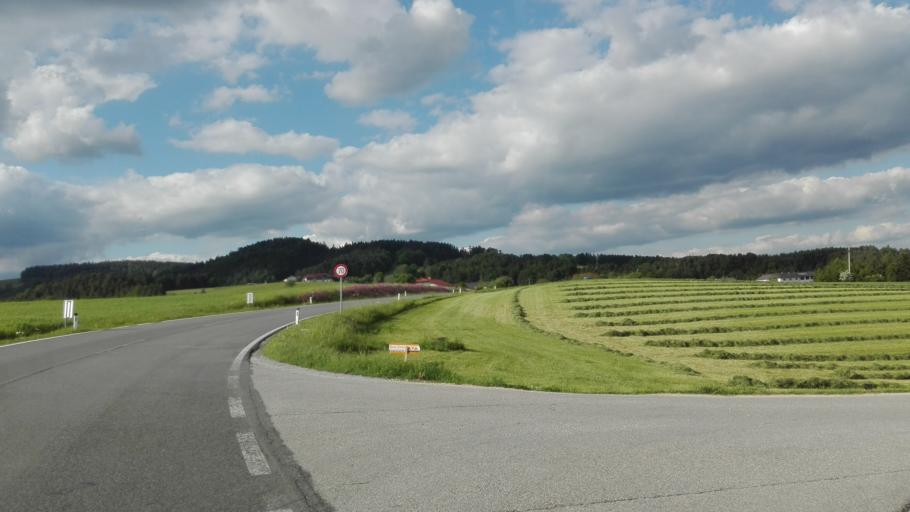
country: AT
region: Upper Austria
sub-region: Politischer Bezirk Perg
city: Perg
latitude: 48.3794
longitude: 14.7032
